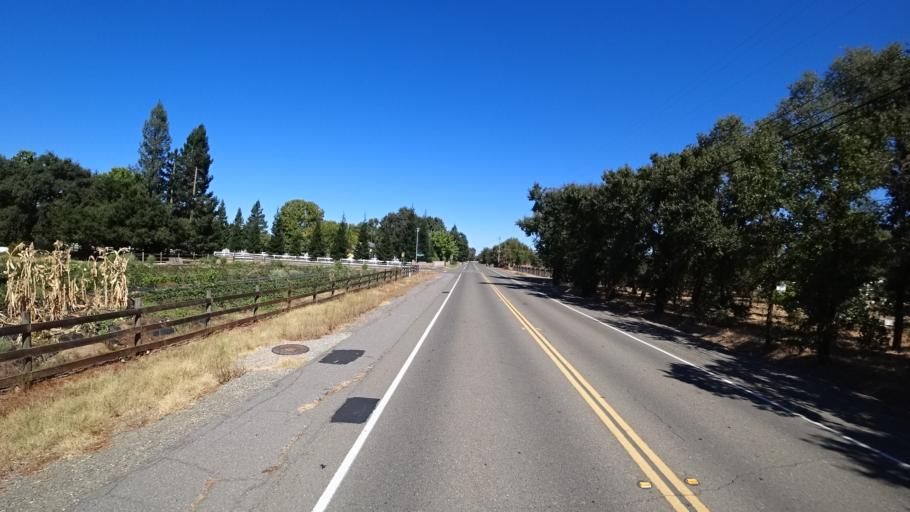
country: US
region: California
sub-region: Sacramento County
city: Vineyard
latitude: 38.4276
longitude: -121.3254
